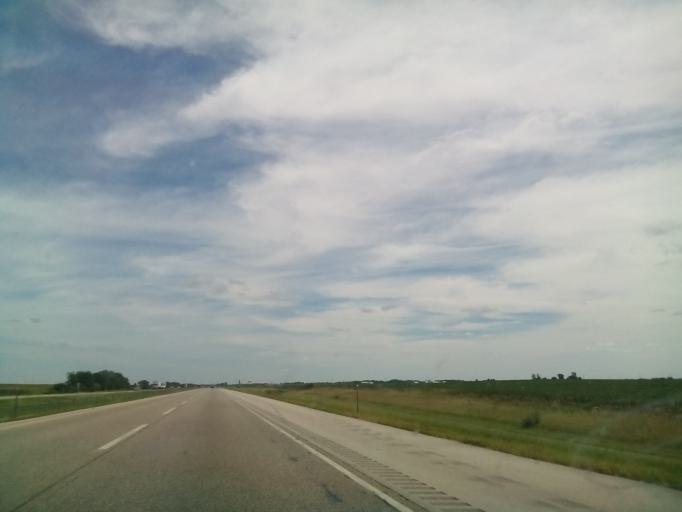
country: US
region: Illinois
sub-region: DeKalb County
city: Malta
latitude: 41.8999
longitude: -88.8283
